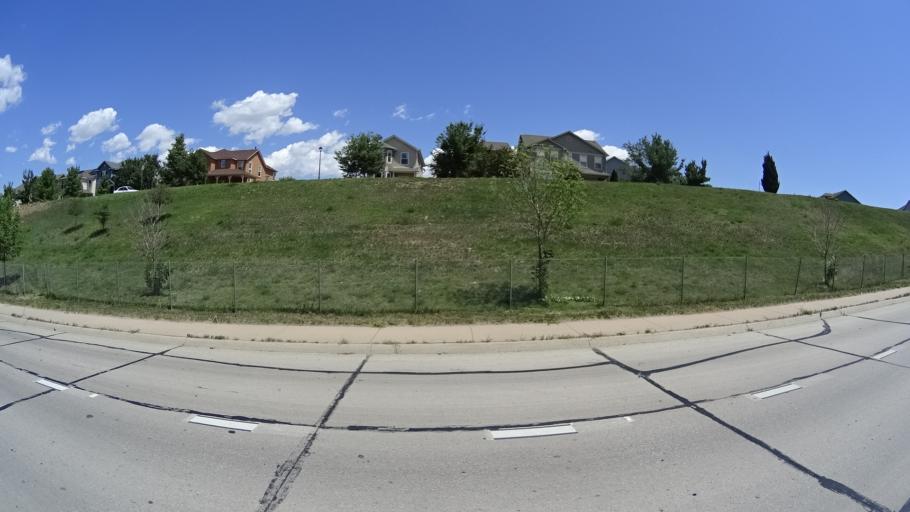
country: US
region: Colorado
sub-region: El Paso County
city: Stratmoor
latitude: 38.8099
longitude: -104.7878
